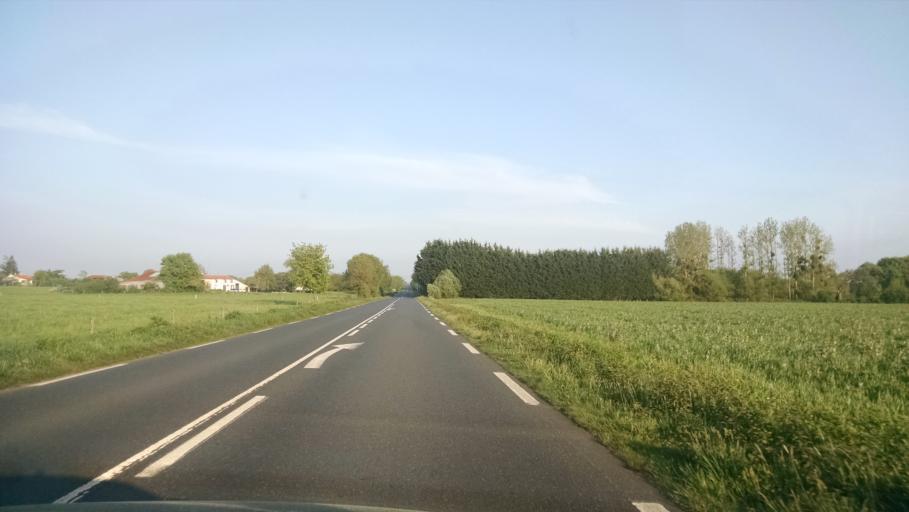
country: FR
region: Pays de la Loire
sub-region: Departement de la Loire-Atlantique
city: Boussay
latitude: 47.0674
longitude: -1.2071
